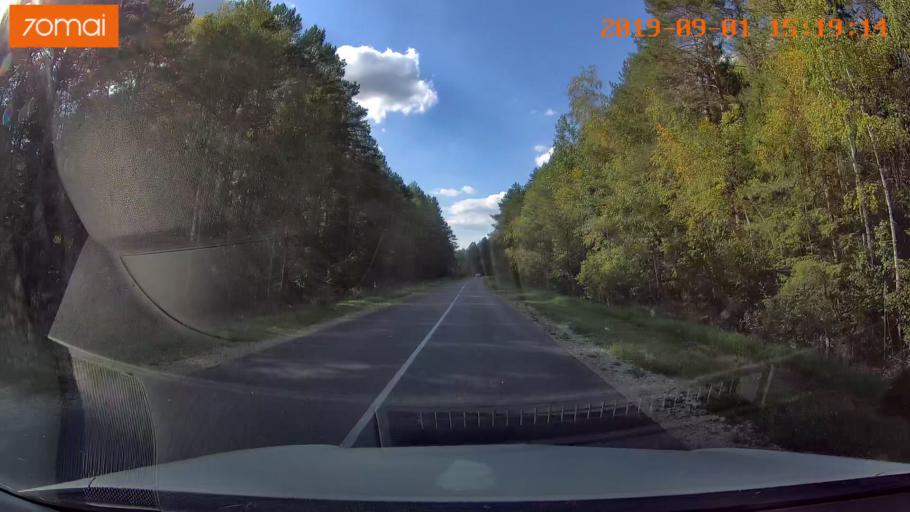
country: RU
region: Kaluga
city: Maloyaroslavets
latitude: 54.9123
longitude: 36.4974
